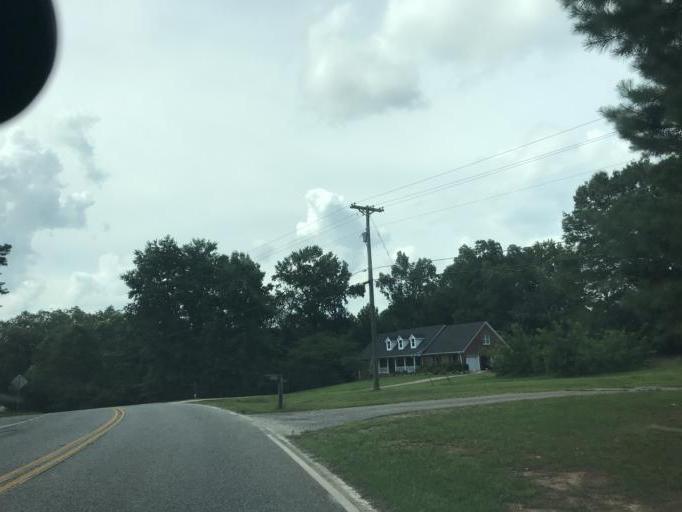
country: US
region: Georgia
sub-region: Forsyth County
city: Cumming
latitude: 34.2108
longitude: -84.2360
